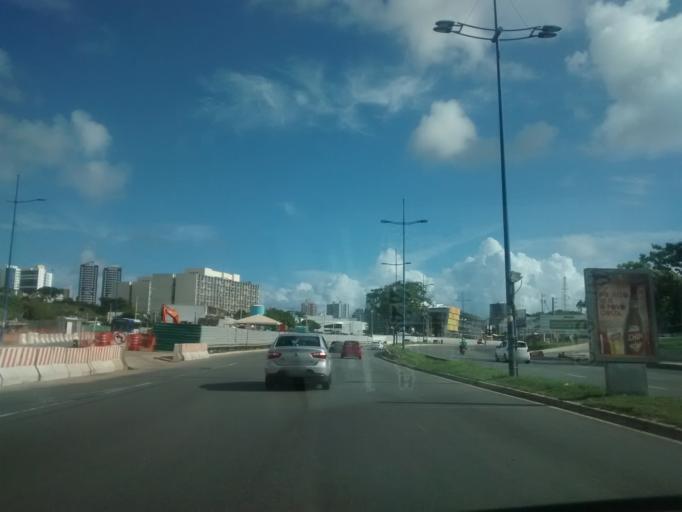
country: BR
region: Bahia
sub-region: Salvador
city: Salvador
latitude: -12.9762
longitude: -38.4614
